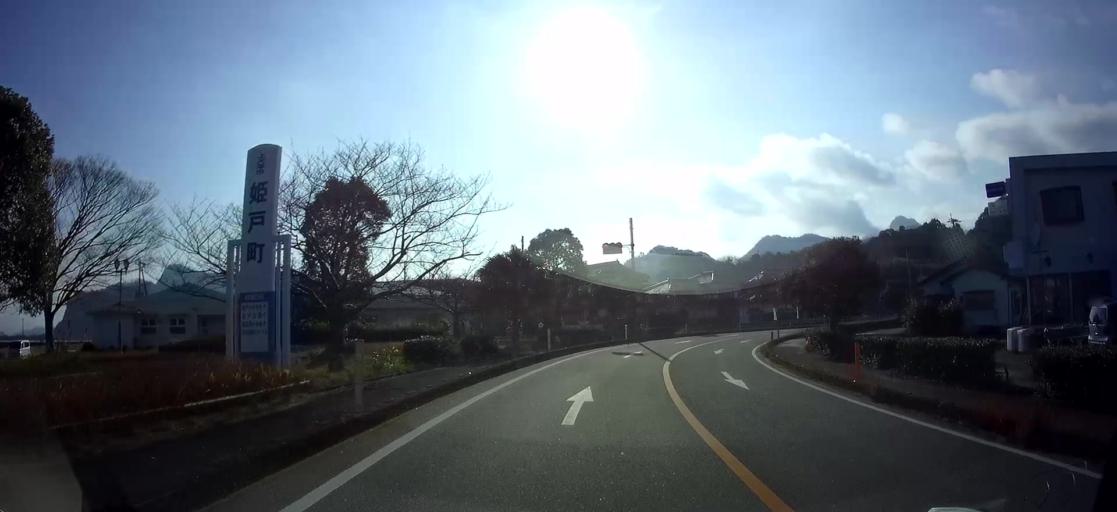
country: JP
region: Kumamoto
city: Yatsushiro
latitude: 32.4428
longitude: 130.4151
